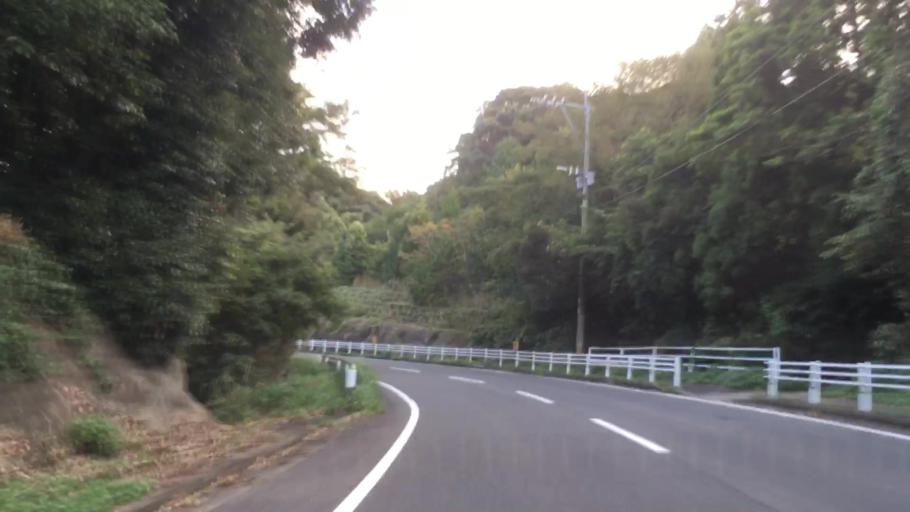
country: JP
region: Nagasaki
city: Sasebo
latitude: 33.0367
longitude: 129.6599
